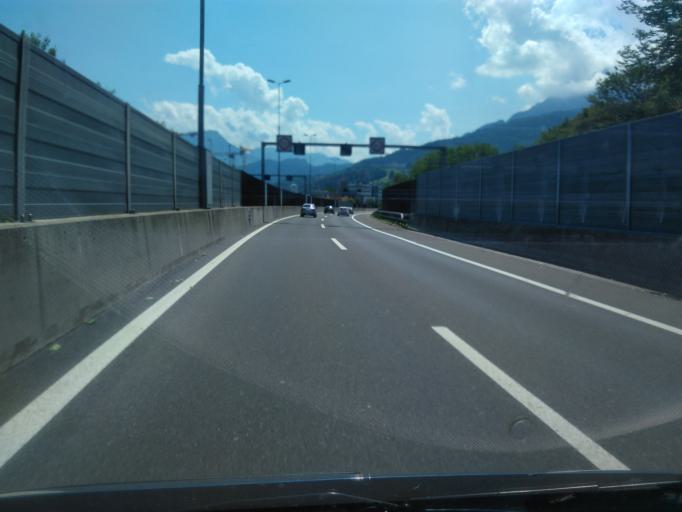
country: CH
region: Lucerne
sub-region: Lucerne-Stadt District
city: Luzern
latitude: 47.0367
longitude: 8.2953
